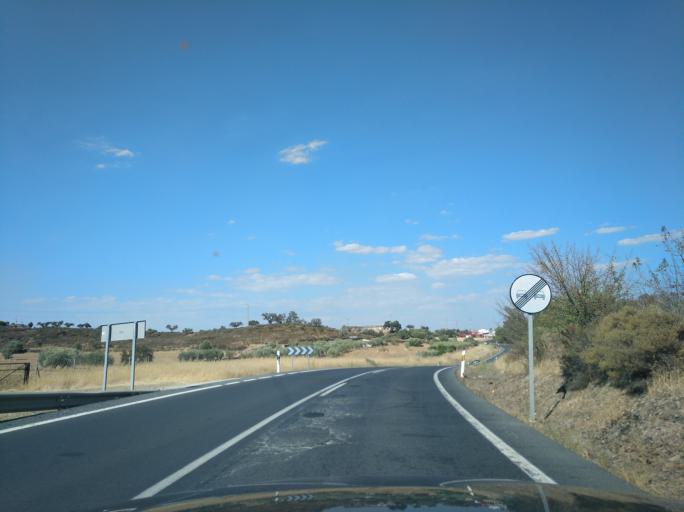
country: ES
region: Andalusia
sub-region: Provincia de Huelva
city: Alosno
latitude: 37.5426
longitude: -7.1278
